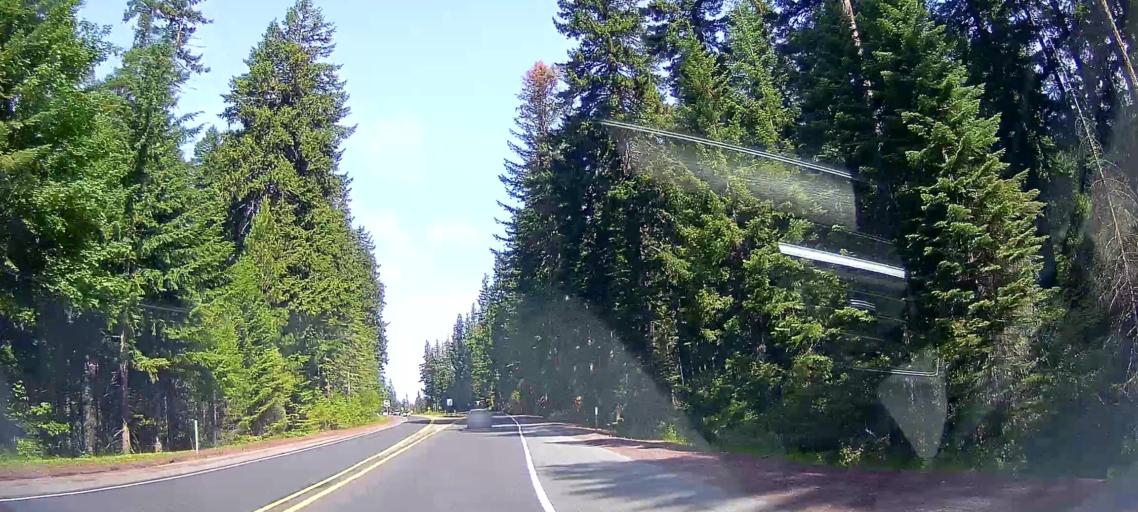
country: US
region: Oregon
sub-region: Clackamas County
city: Mount Hood Village
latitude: 45.1285
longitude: -121.5969
